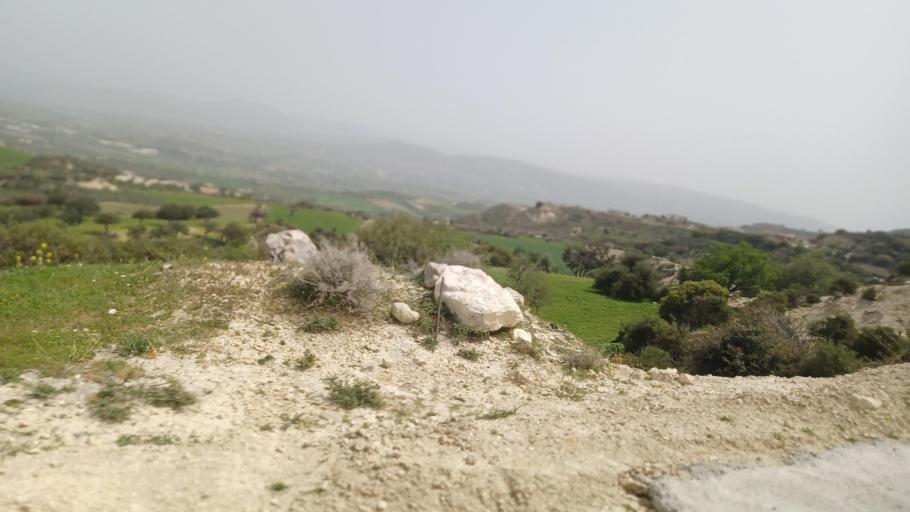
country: CY
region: Pafos
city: Polis
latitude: 35.0043
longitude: 32.3990
